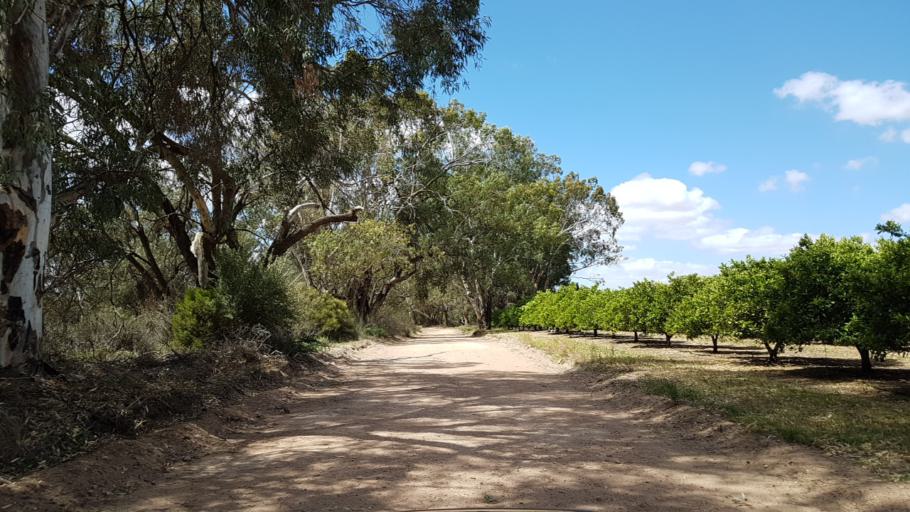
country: AU
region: South Australia
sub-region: Loxton Waikerie
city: Waikerie
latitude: -34.1777
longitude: 140.0196
